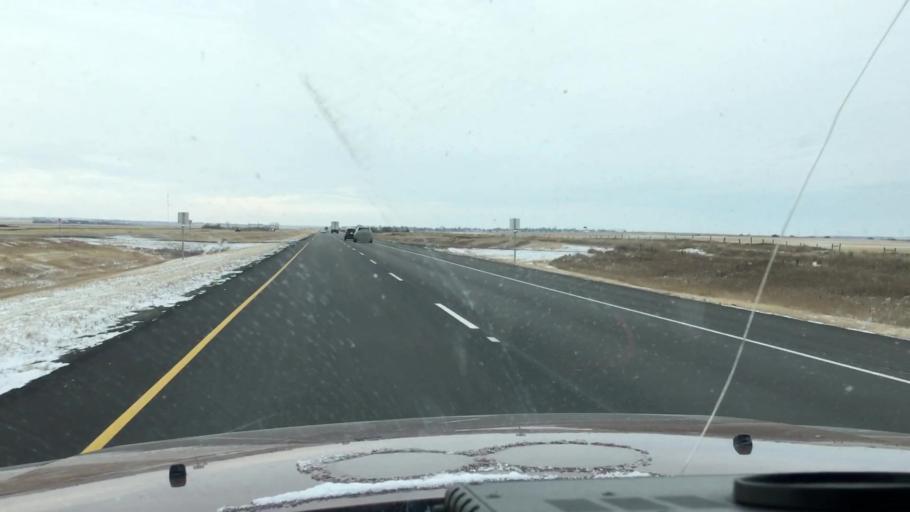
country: CA
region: Saskatchewan
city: Saskatoon
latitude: 51.8390
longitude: -106.5041
